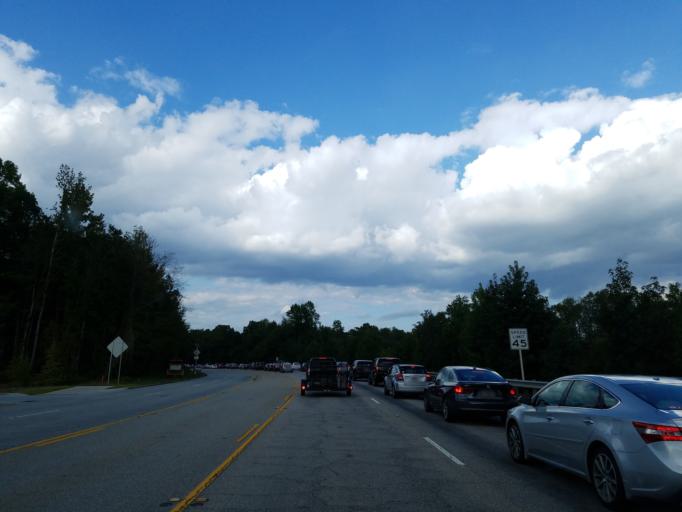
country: US
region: South Carolina
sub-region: Greenville County
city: Mauldin
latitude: 34.8305
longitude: -82.3178
